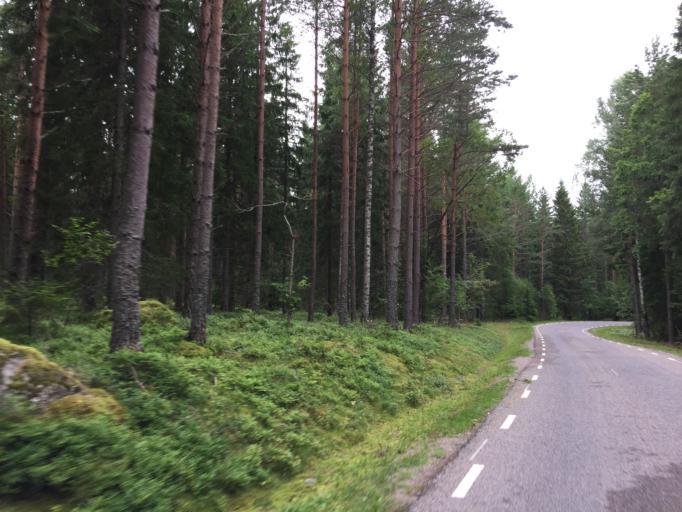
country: SE
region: Soedermanland
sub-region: Vingakers Kommun
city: Vingaker
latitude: 59.0080
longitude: 15.7277
